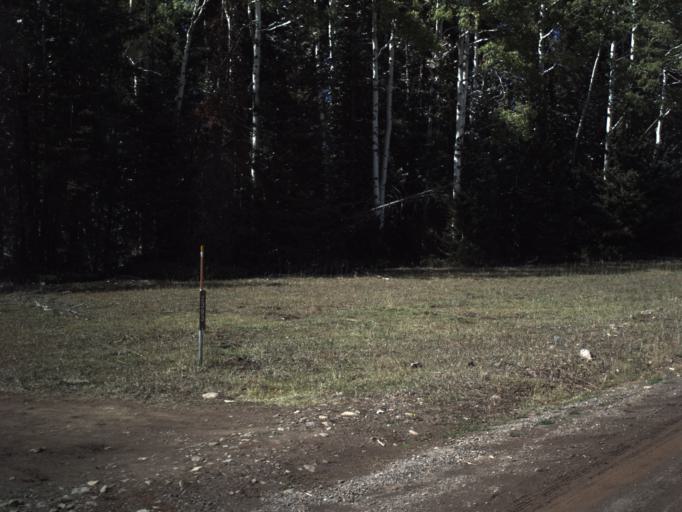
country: US
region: Utah
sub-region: Piute County
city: Junction
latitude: 38.2492
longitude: -112.3740
